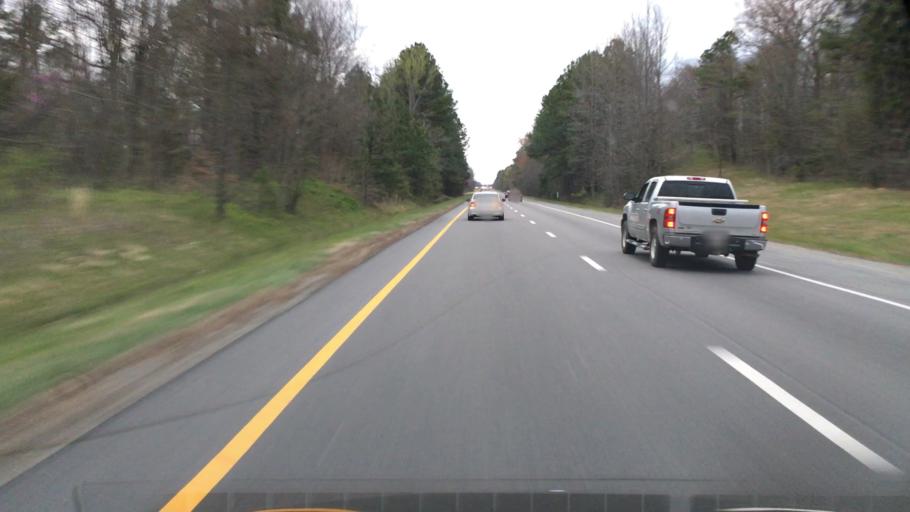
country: US
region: Virginia
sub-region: Sussex County
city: Sussex
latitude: 36.8840
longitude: -77.4023
